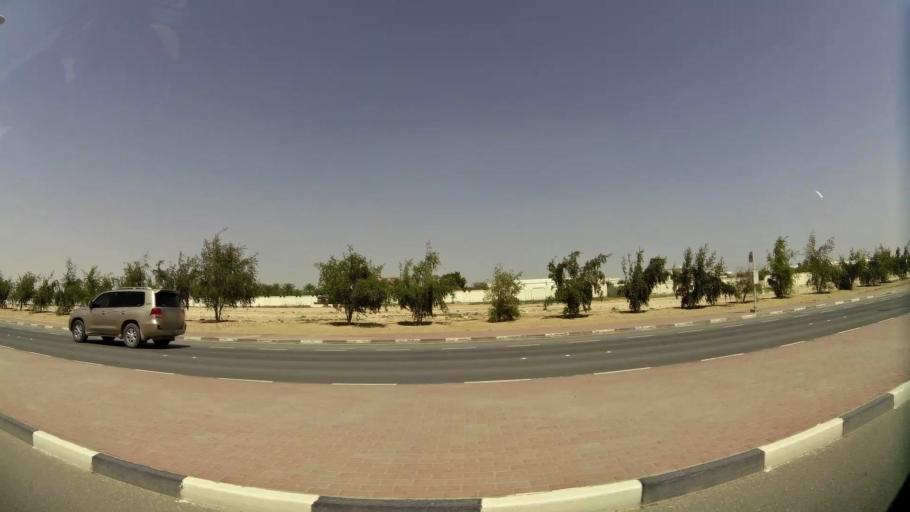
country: QA
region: Baladiyat Umm Salal
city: Umm Salal Muhammad
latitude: 25.3849
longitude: 51.4251
